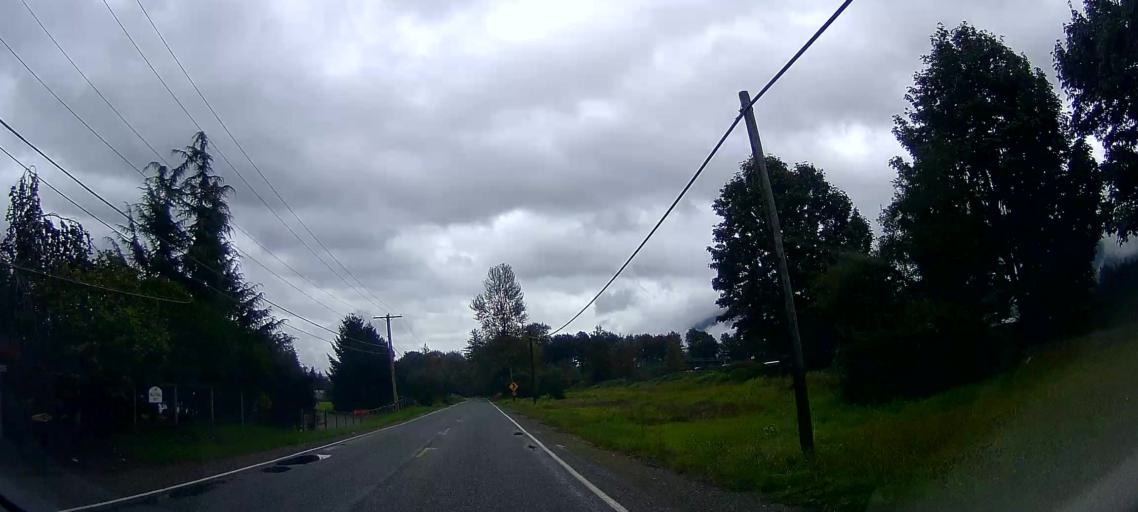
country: US
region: Washington
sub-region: Skagit County
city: Sedro-Woolley
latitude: 48.5269
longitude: -122.0319
